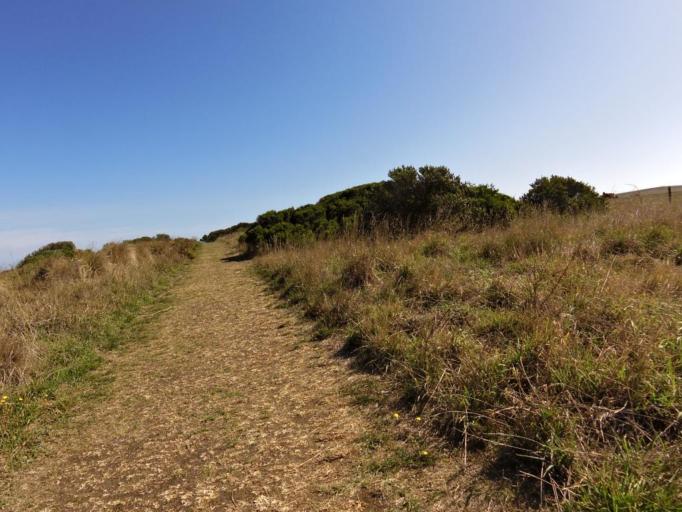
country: AU
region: Victoria
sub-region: Bass Coast
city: North Wonthaggi
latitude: -38.5361
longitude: 145.4213
